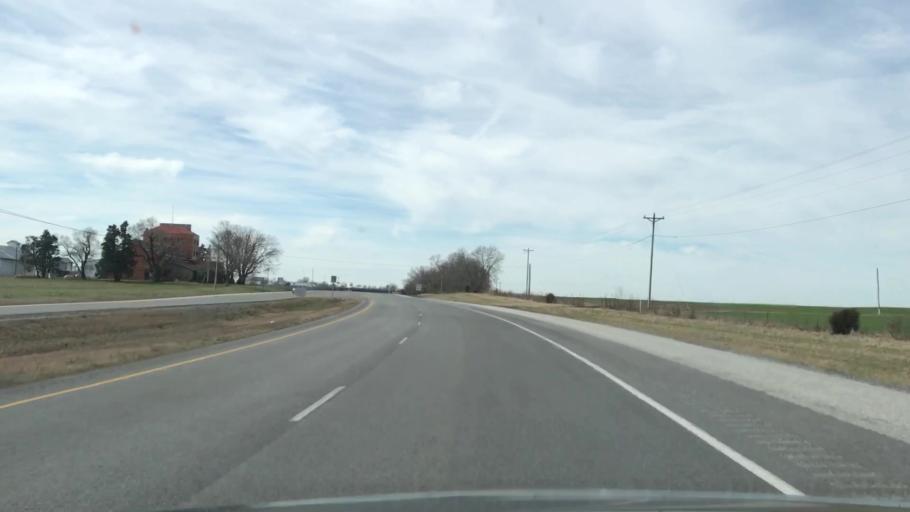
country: US
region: Kentucky
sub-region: Trigg County
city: Cadiz
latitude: 36.8867
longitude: -87.7286
